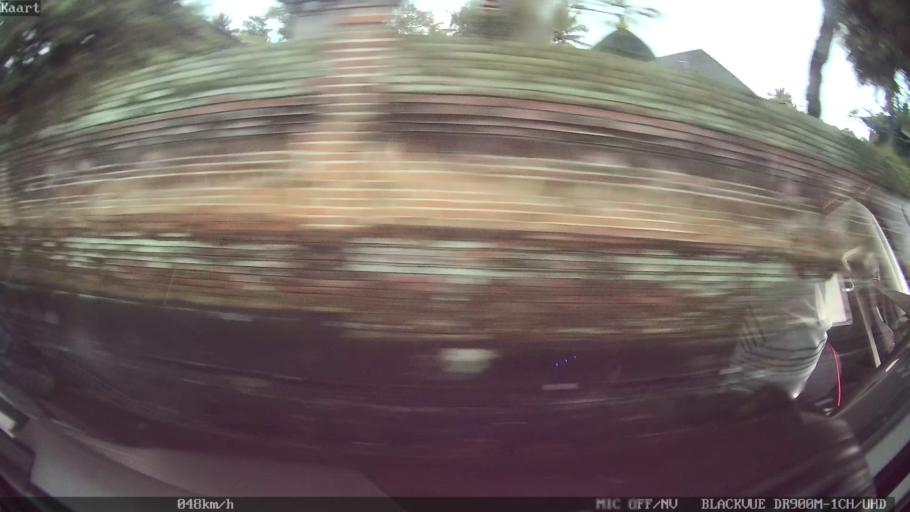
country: ID
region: Bali
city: Banjar Teguan
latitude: -8.5187
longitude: 115.2289
